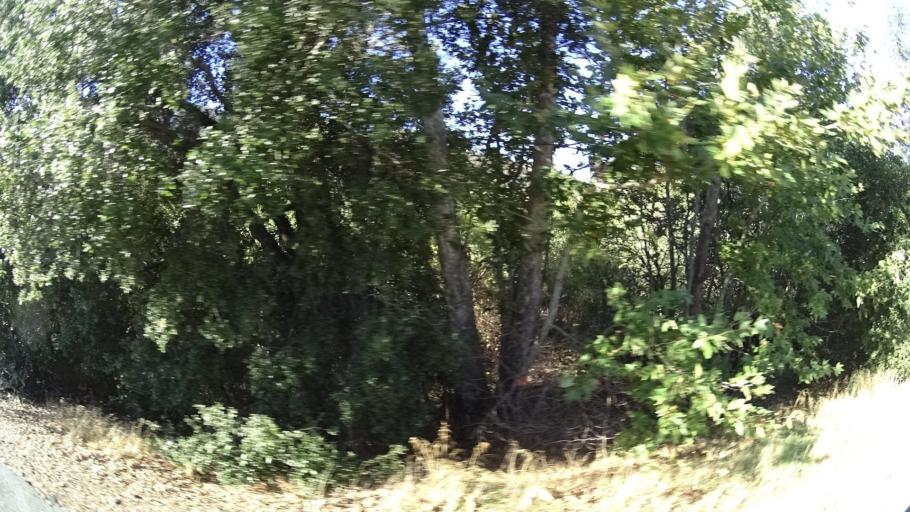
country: MX
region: Baja California
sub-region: Tecate
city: Lomas de Santa Anita
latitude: 32.6088
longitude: -116.6962
